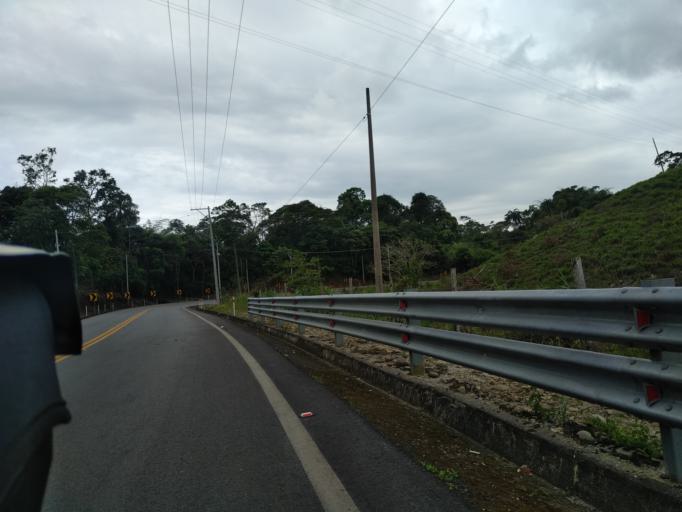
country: EC
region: Pastaza
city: Puyo
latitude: -1.3089
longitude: -77.8847
